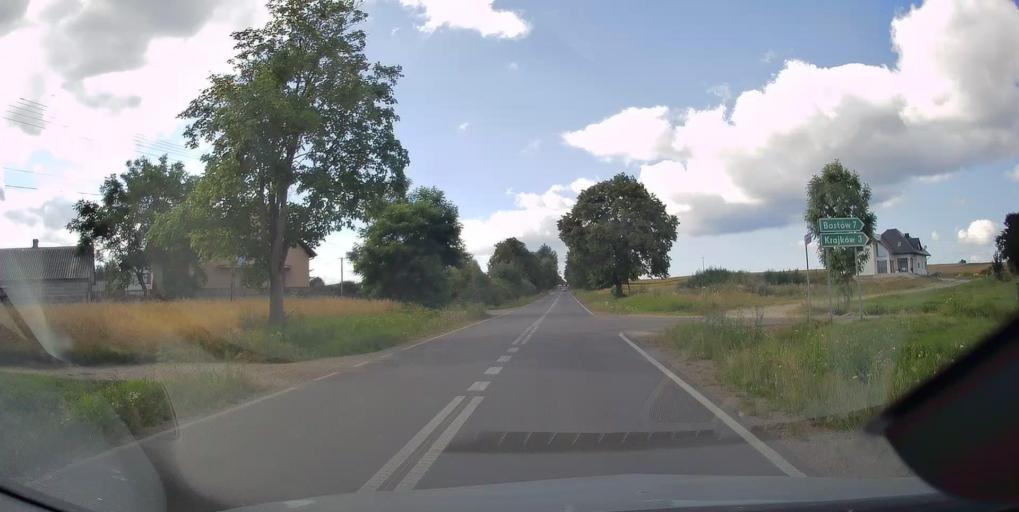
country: PL
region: Swietokrzyskie
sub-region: Powiat kielecki
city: Bodzentyn
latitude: 50.9185
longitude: 20.9921
